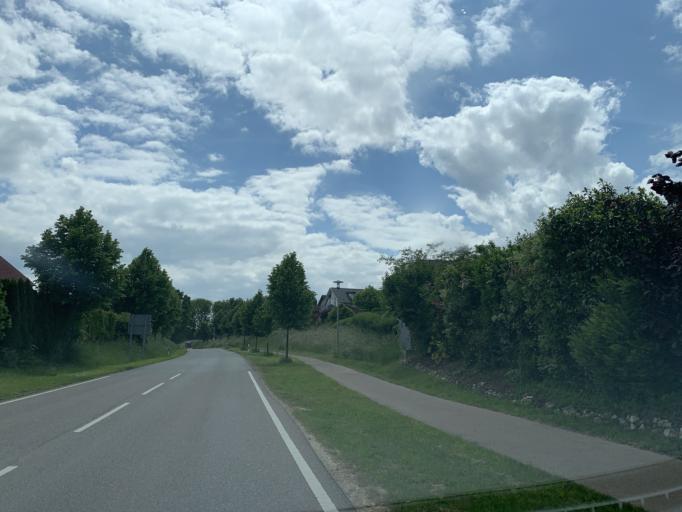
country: DE
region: Baden-Wuerttemberg
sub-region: Tuebingen Region
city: Staig
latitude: 48.3031
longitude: 9.9913
